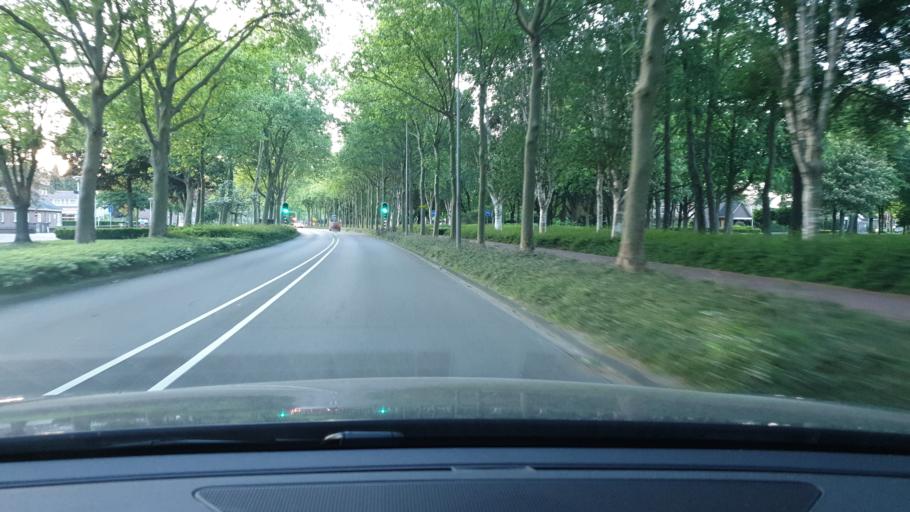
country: NL
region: North Brabant
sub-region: Gemeente Valkenswaard
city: Valkenswaard
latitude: 51.3544
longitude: 5.4515
